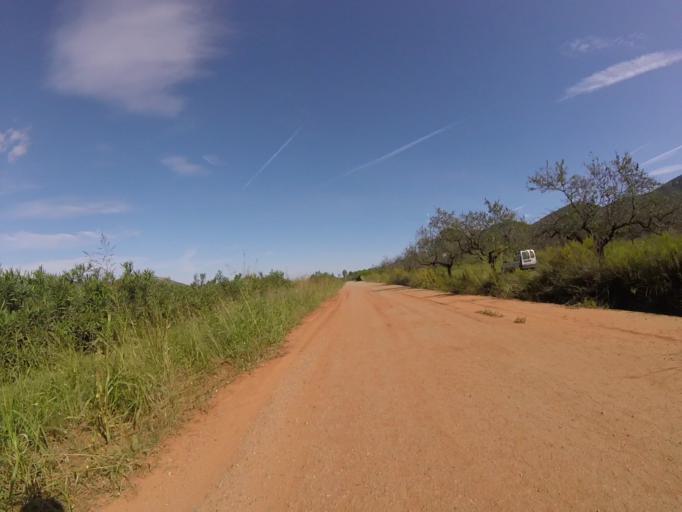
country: ES
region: Valencia
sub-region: Provincia de Castello
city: Santa Magdalena de Pulpis
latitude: 40.3792
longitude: 0.3350
